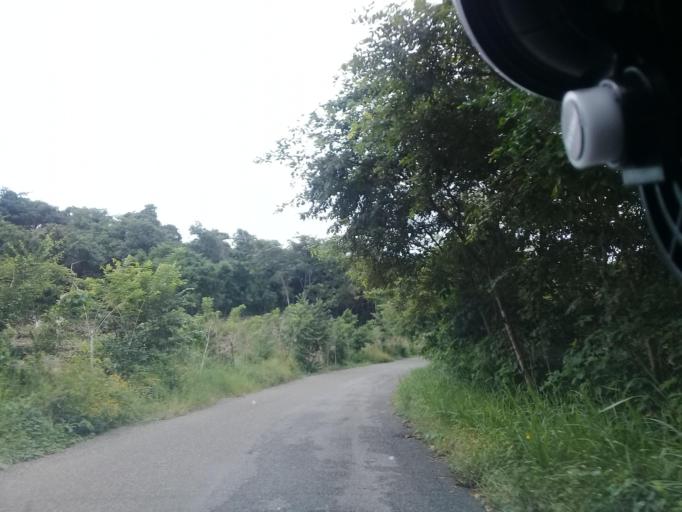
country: MX
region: Hidalgo
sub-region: Huejutla de Reyes
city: Chalahuiyapa
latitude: 21.2052
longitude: -98.3561
